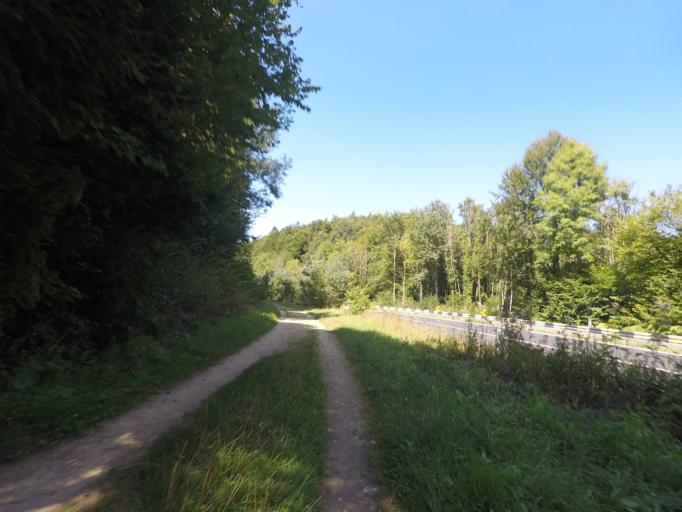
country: LU
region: Luxembourg
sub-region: Canton de Luxembourg
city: Strassen
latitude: 49.6314
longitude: 6.0898
